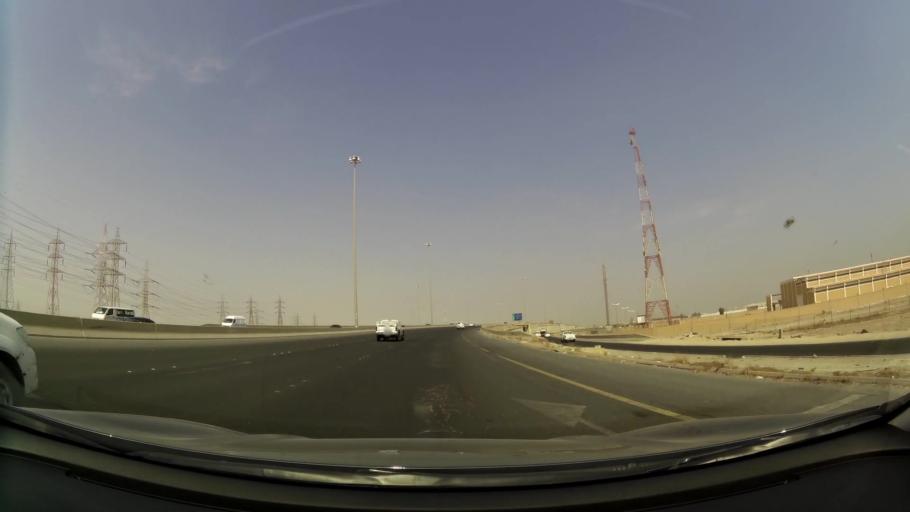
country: KW
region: Al Ahmadi
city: Al Ahmadi
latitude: 29.0578
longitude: 48.1087
